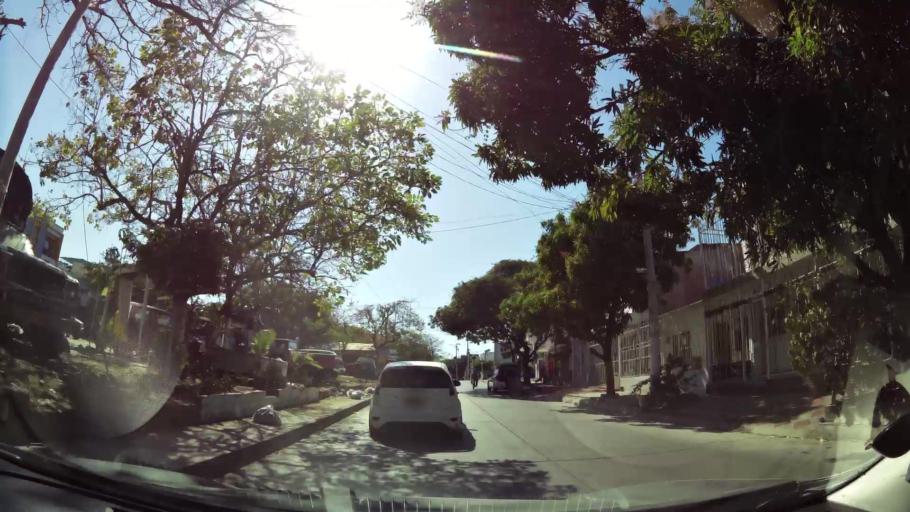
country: CO
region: Atlantico
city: Soledad
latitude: 10.9312
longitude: -74.7866
